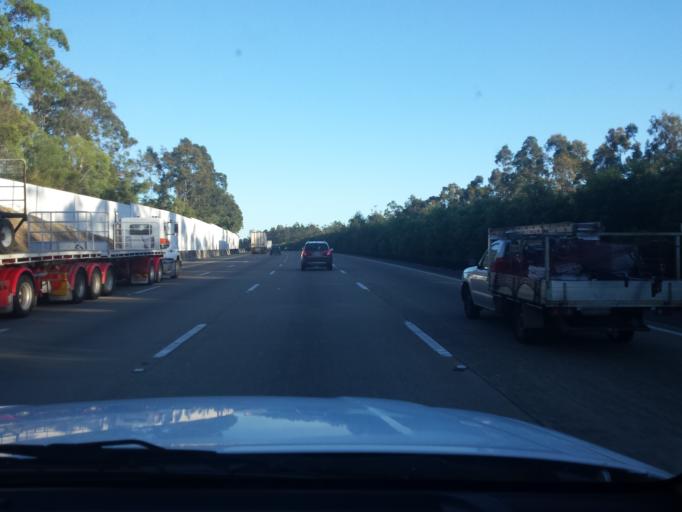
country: AU
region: Queensland
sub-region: Gold Coast
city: Ormeau Hills
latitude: -27.8289
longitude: 153.2998
